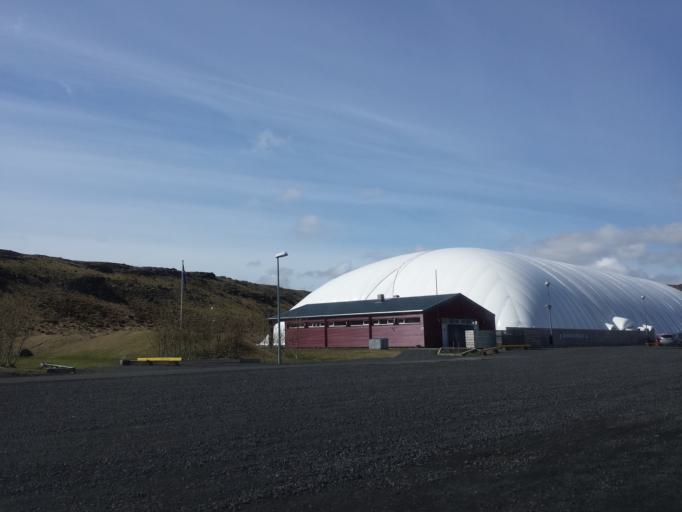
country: IS
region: South
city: Hveragerdi
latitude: 64.0109
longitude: -21.1923
